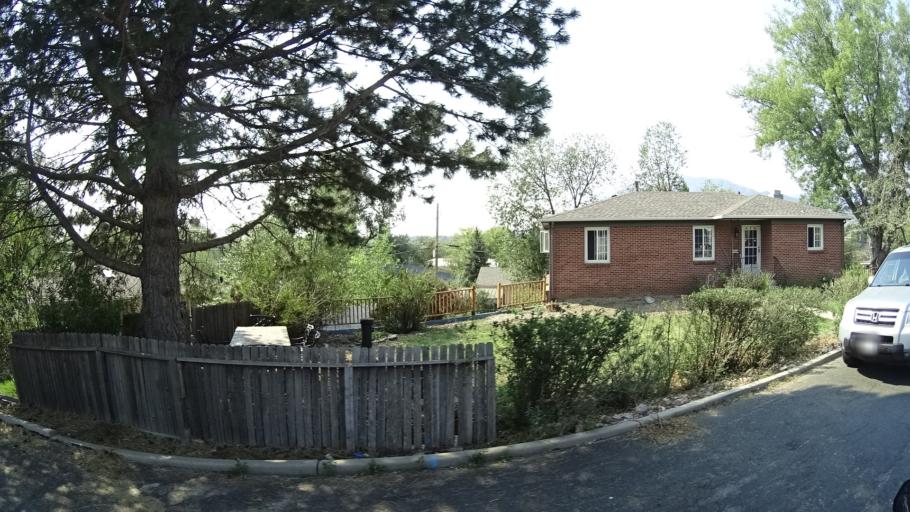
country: US
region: Colorado
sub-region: El Paso County
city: Colorado Springs
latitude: 38.8134
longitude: -104.8384
